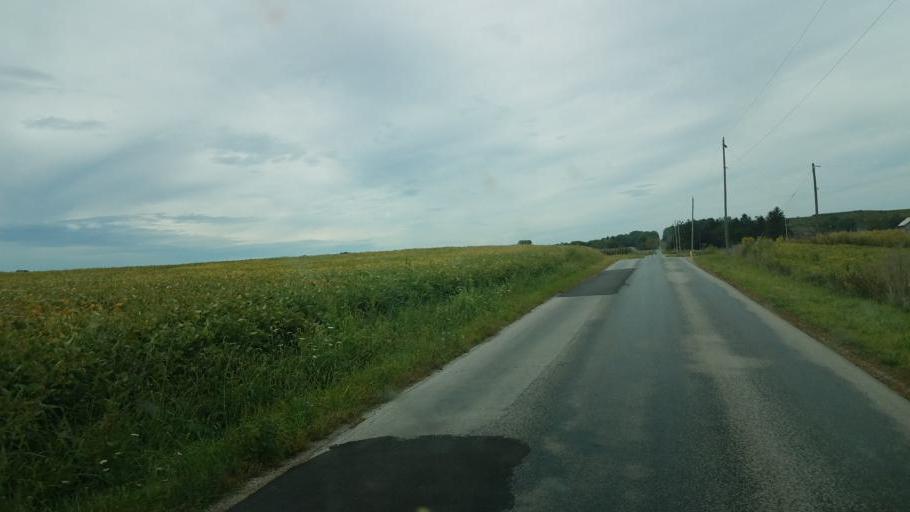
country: US
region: Ohio
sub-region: Knox County
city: Centerburg
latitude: 40.3207
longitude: -82.7073
